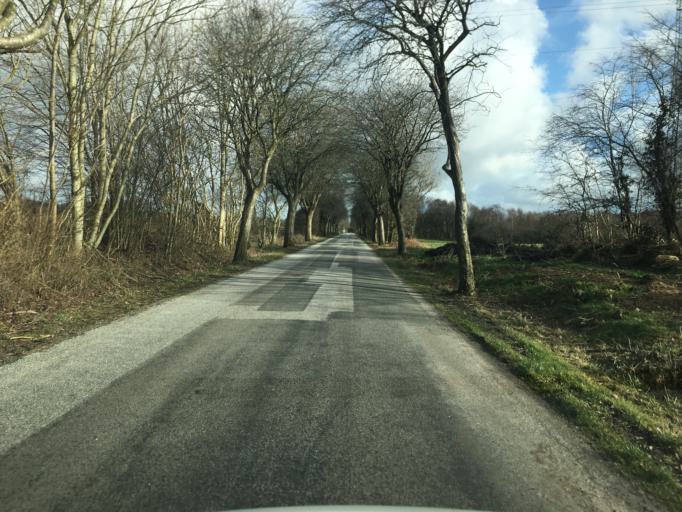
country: DK
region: South Denmark
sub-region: Aabenraa Kommune
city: Krusa
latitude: 54.9009
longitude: 9.4110
